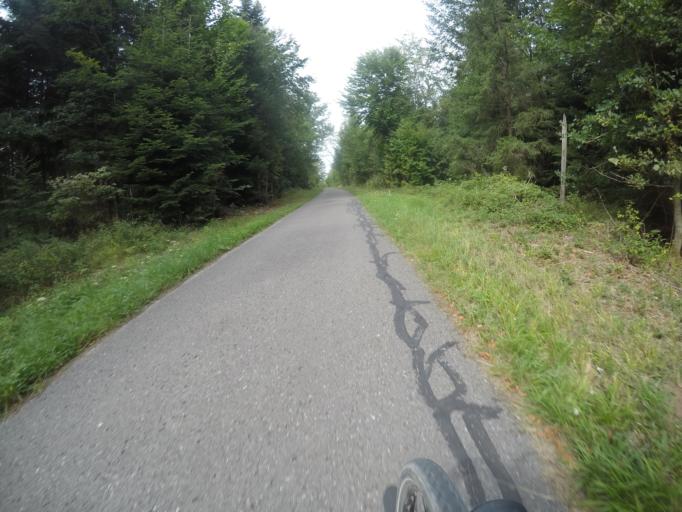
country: DE
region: Baden-Wuerttemberg
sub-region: Karlsruhe Region
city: Wurmberg
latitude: 48.8695
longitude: 8.7727
